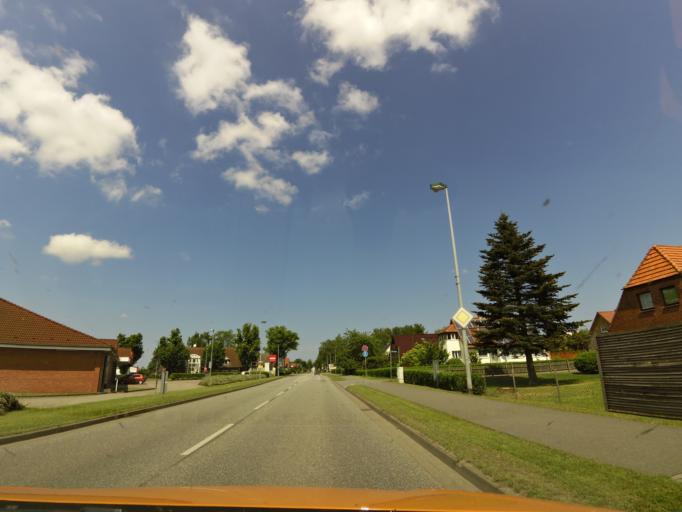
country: DE
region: Mecklenburg-Vorpommern
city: Rehna
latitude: 53.7738
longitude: 11.0516
